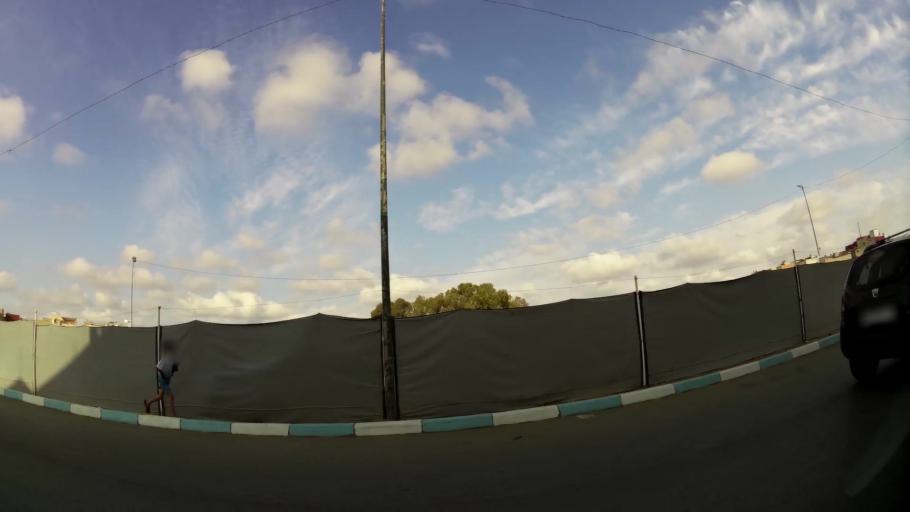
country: MA
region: Rabat-Sale-Zemmour-Zaer
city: Sale
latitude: 34.0486
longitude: -6.7766
